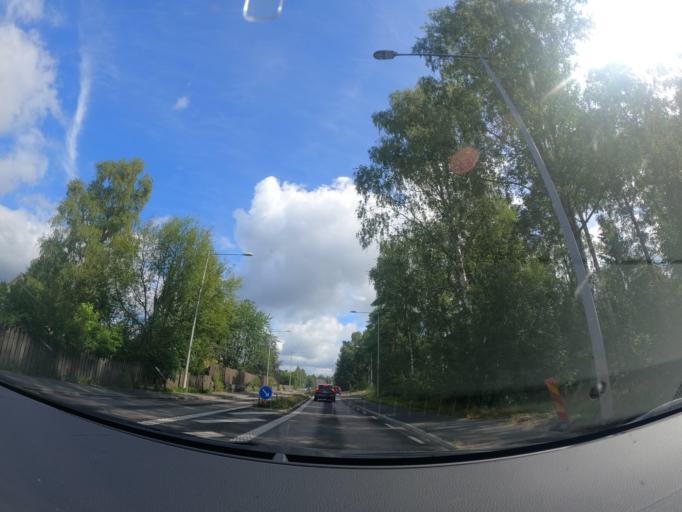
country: SE
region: Joenkoeping
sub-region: Gislaveds Kommun
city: Smalandsstenar
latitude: 57.1508
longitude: 13.3975
